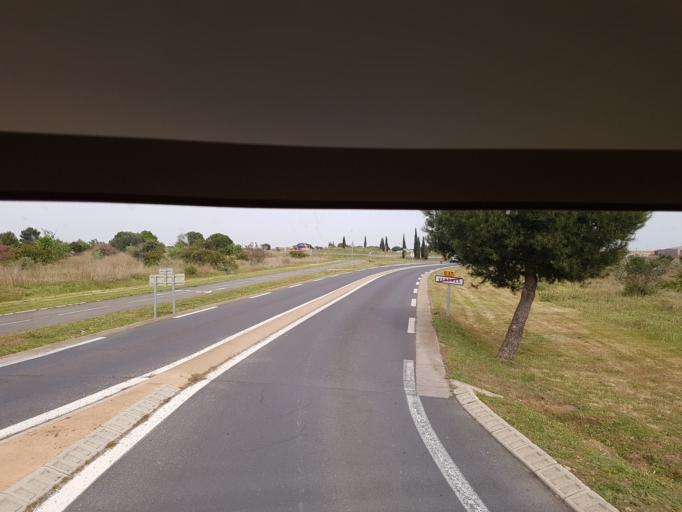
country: FR
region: Languedoc-Roussillon
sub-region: Departement de l'Herault
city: Vendres
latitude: 43.2697
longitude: 3.2330
